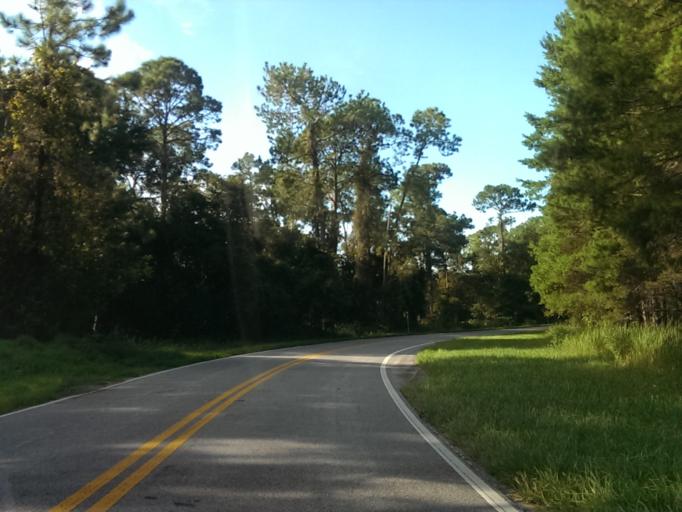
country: US
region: Florida
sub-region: Polk County
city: Citrus Ridge
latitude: 28.4209
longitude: -81.6182
